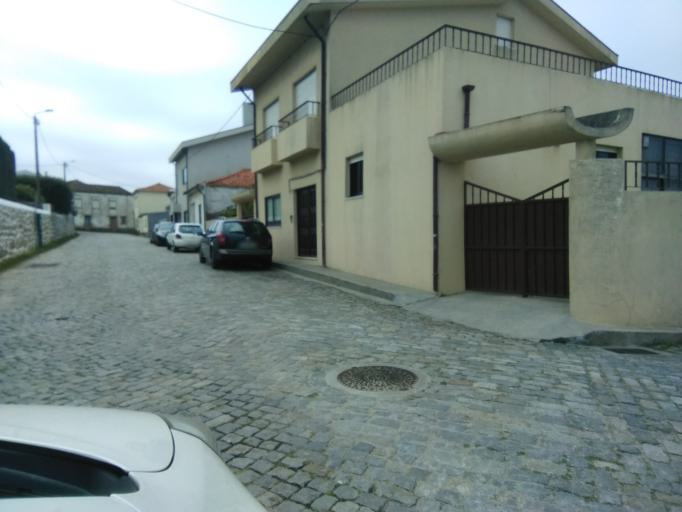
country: PT
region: Porto
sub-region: Matosinhos
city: Lavra
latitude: 41.2330
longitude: -8.7149
